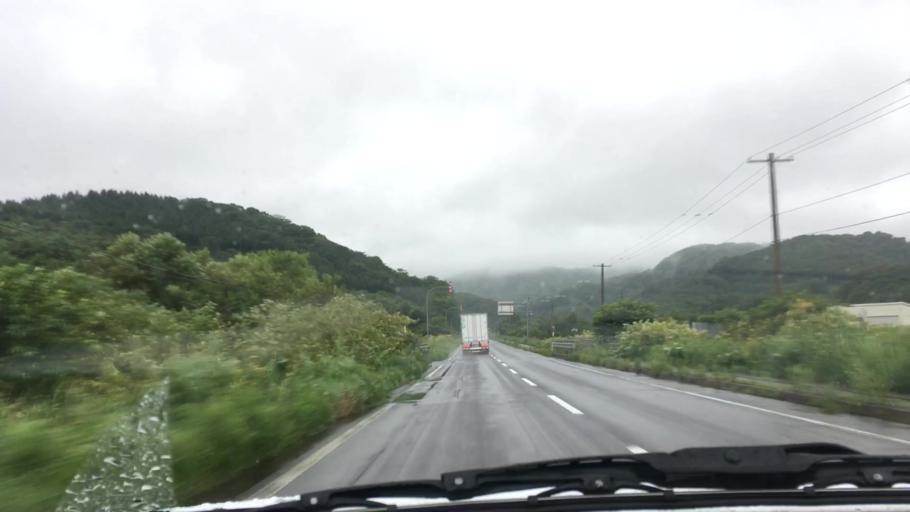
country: JP
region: Hokkaido
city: Niseko Town
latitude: 42.5995
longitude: 140.6323
